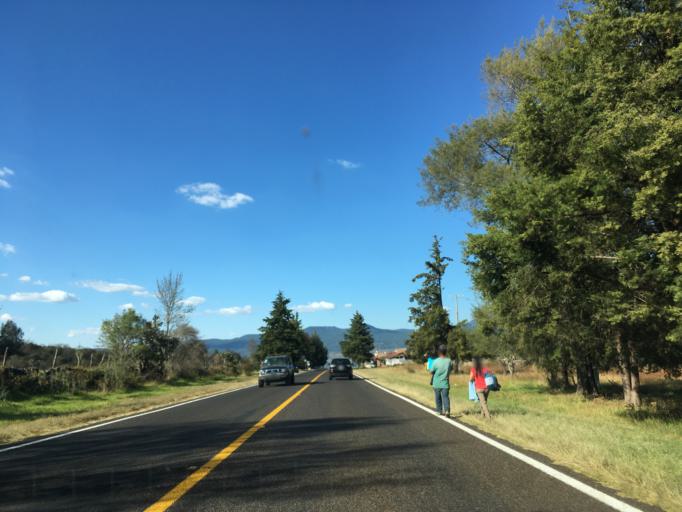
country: MX
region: Michoacan
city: Tzintzuntzan
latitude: 19.6103
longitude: -101.5768
